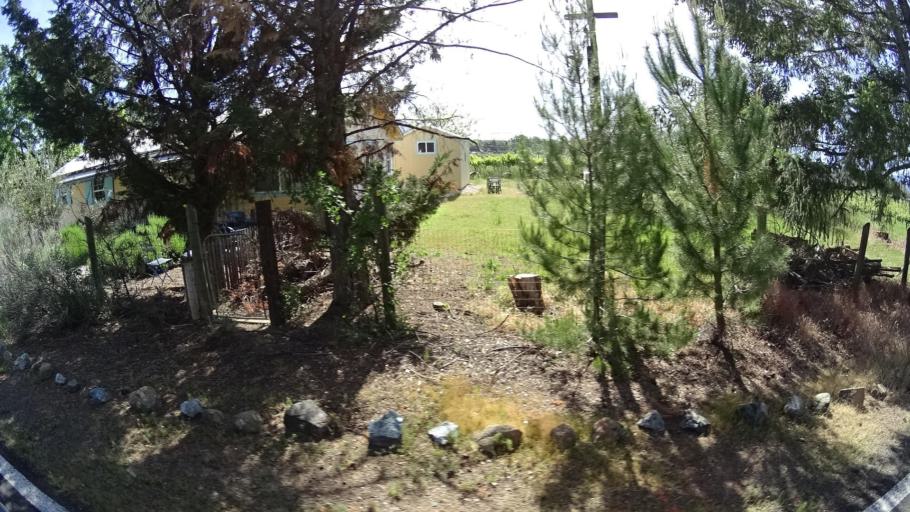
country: US
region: California
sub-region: Lake County
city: Kelseyville
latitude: 38.9567
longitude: -122.8962
